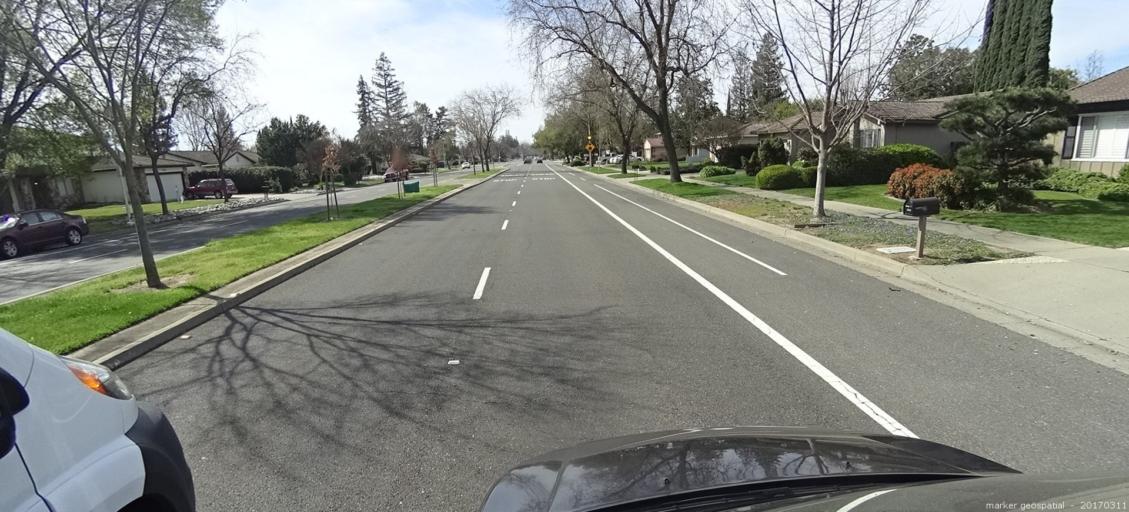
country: US
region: California
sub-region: Yolo County
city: West Sacramento
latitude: 38.5043
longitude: -121.5462
